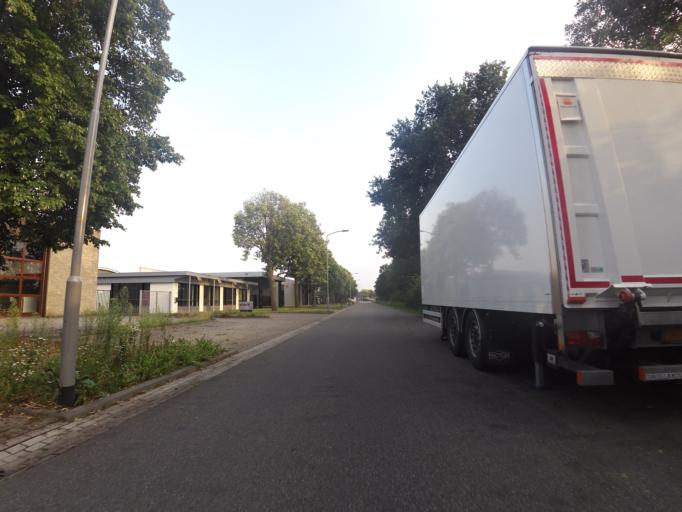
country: NL
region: Gelderland
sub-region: Oude IJsselstreek
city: Gendringen
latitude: 51.8823
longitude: 6.3820
